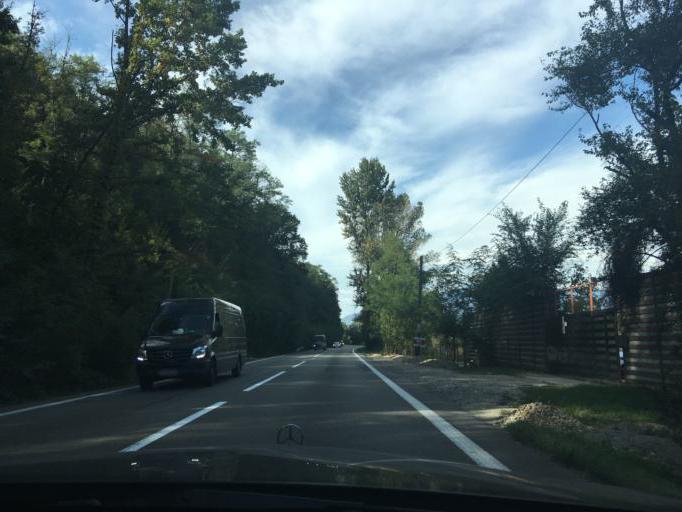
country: RO
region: Valcea
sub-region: Comuna Daesti
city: Daesti
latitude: 45.2017
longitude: 24.3752
